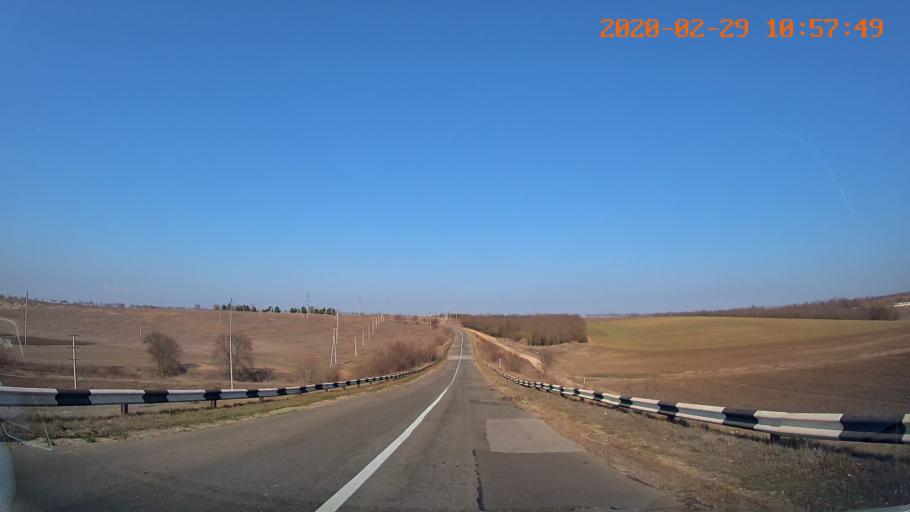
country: MD
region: Telenesti
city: Grigoriopol
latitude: 47.1637
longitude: 29.3201
